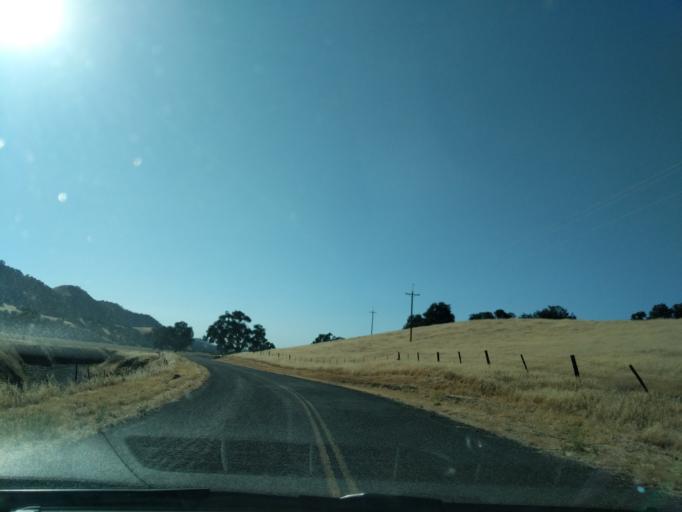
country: US
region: California
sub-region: Monterey County
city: King City
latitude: 36.1699
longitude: -120.7866
